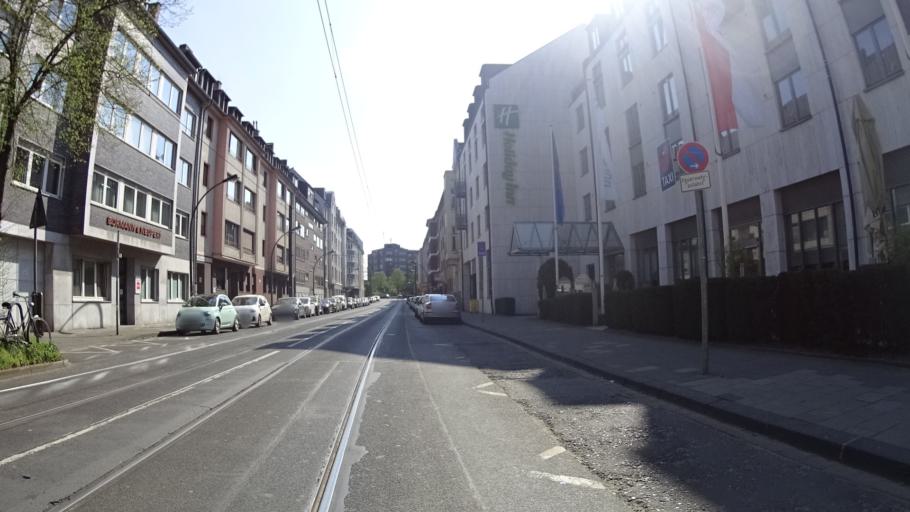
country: DE
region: North Rhine-Westphalia
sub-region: Regierungsbezirk Dusseldorf
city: Dusseldorf
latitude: 51.2092
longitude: 6.7617
